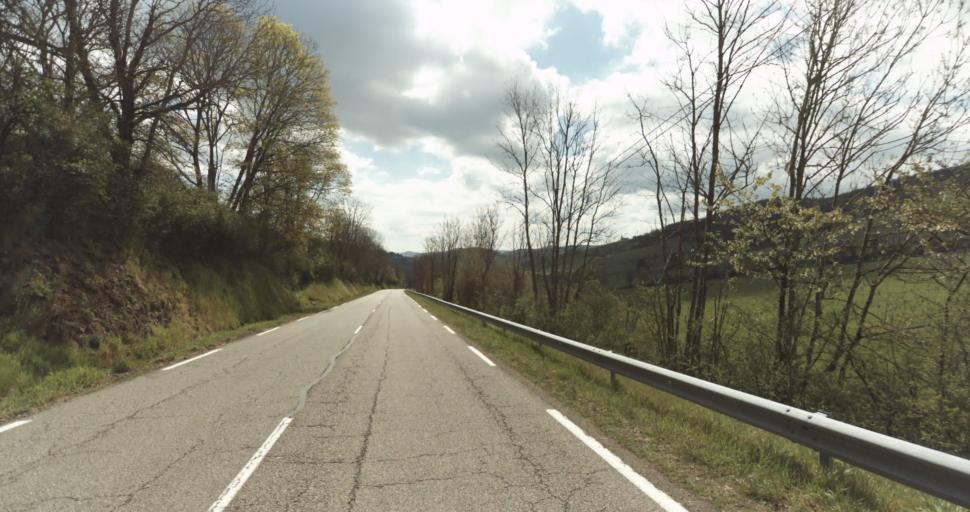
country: FR
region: Rhone-Alpes
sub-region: Departement du Rhone
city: Tarare
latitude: 45.9167
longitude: 4.4174
